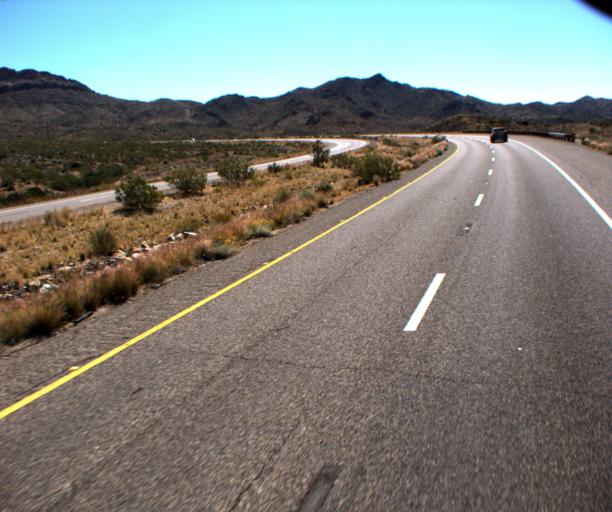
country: US
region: Nevada
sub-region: Clark County
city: Laughlin
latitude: 35.1953
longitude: -114.4129
